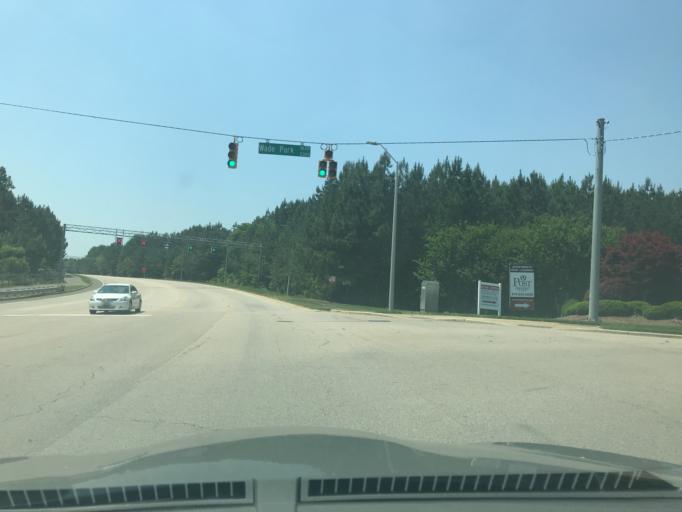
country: US
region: North Carolina
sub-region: Wake County
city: Cary
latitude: 35.8047
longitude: -78.7262
